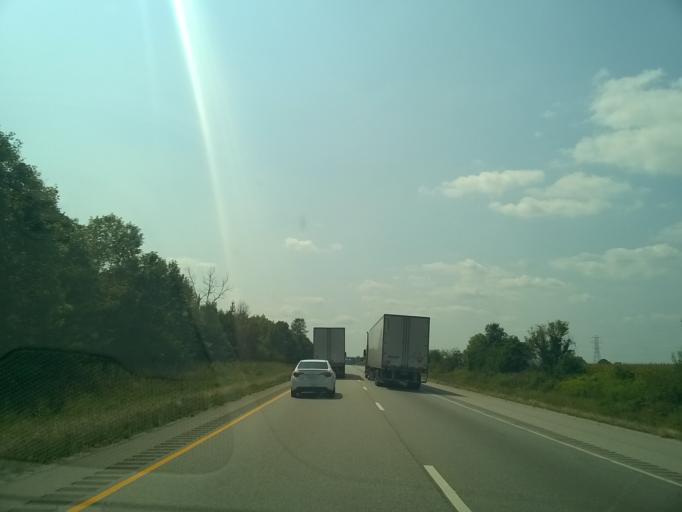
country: US
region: Indiana
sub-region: Vigo County
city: Seelyville
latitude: 39.4342
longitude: -87.2925
